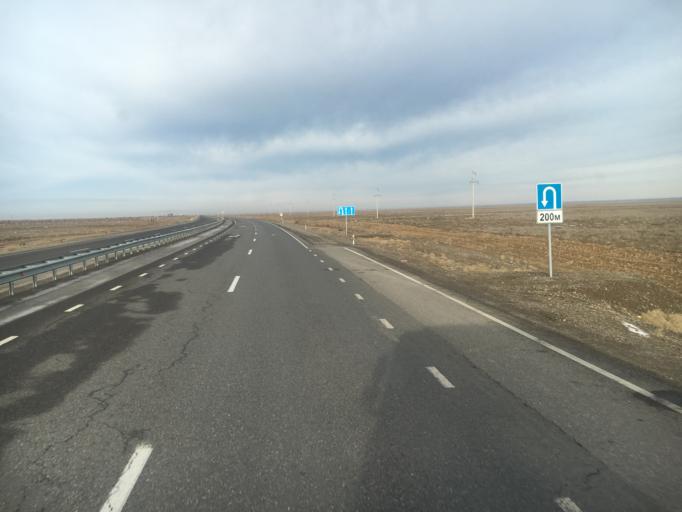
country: KZ
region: Ongtustik Qazaqstan
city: Turkestan
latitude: 43.5010
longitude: 67.8445
